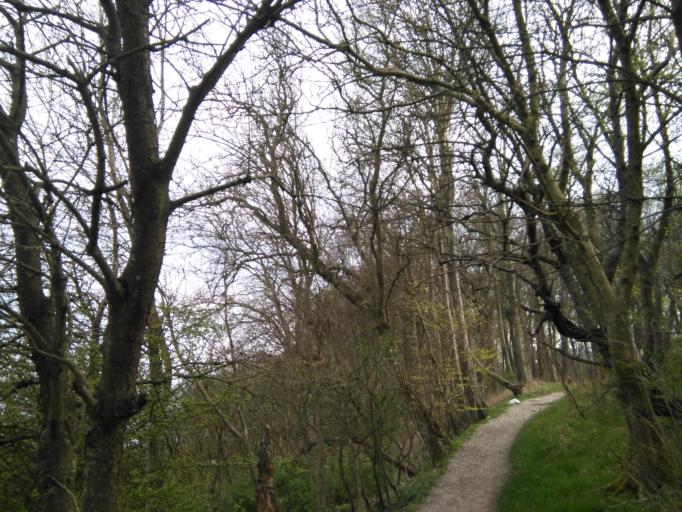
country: DK
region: Central Jutland
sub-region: Arhus Kommune
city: Beder
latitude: 56.0843
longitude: 10.2487
